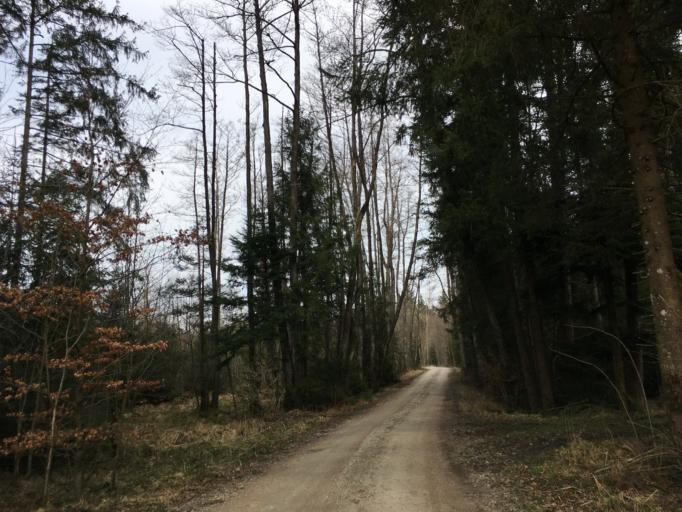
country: DE
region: Bavaria
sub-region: Upper Bavaria
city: Seeon-Seebruck
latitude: 47.9545
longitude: 12.4281
